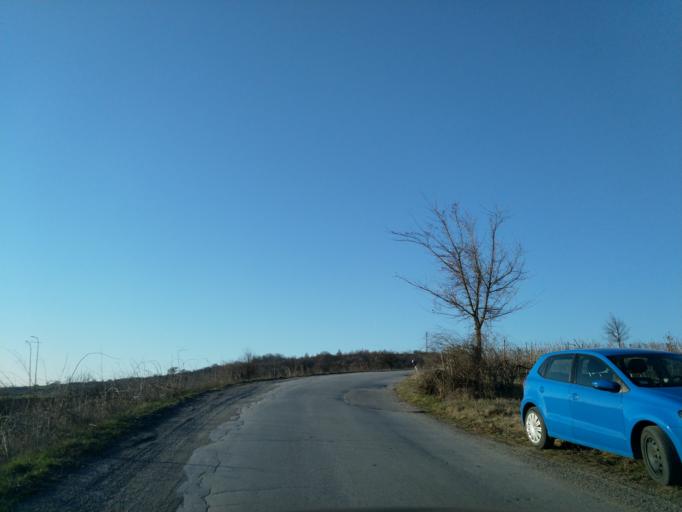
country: RS
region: Central Serbia
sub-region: Pomoravski Okrug
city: Paracin
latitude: 43.9251
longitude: 21.5113
